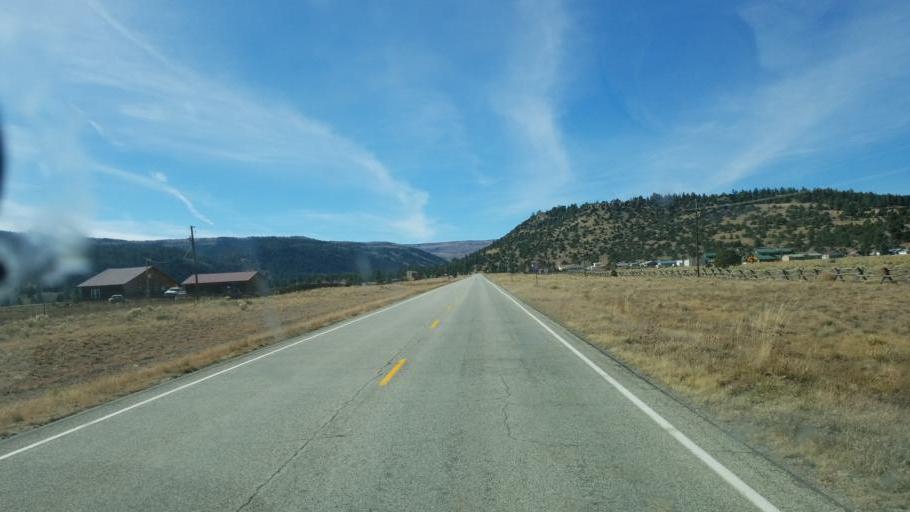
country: US
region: Colorado
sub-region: Conejos County
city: Conejos
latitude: 37.0676
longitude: -106.2158
